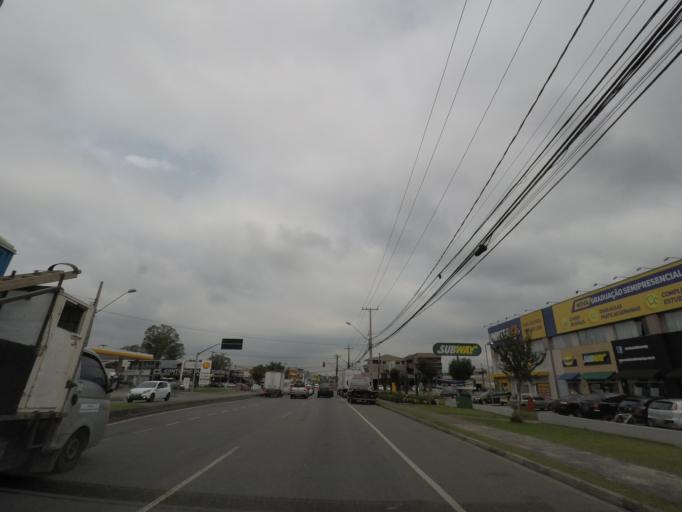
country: BR
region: Parana
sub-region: Curitiba
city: Curitiba
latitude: -25.5110
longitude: -49.3321
